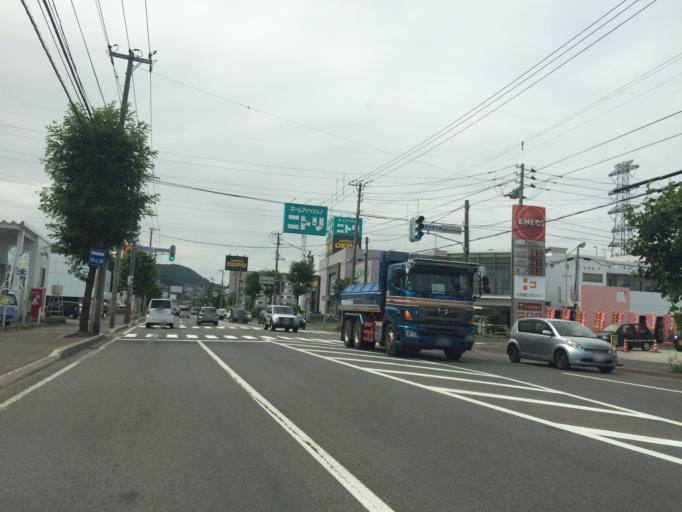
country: JP
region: Hokkaido
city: Sapporo
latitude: 43.0959
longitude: 141.2599
